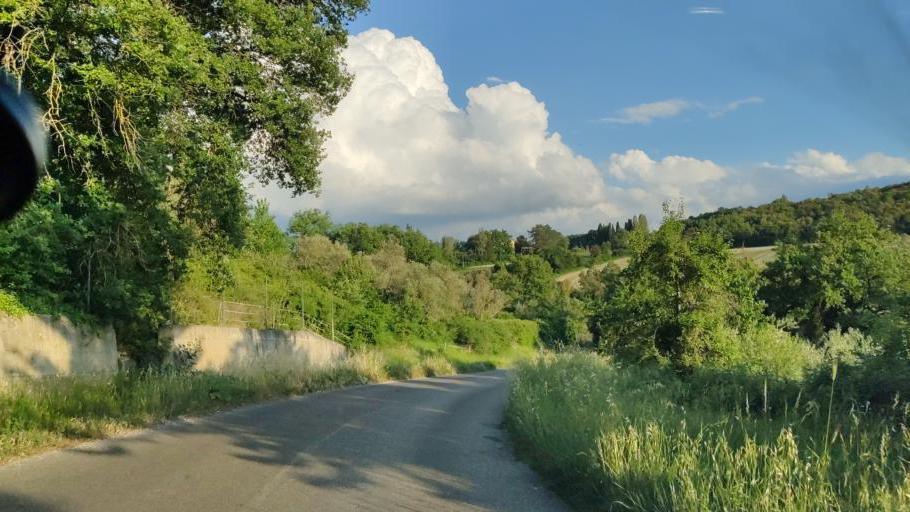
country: IT
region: Umbria
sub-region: Provincia di Terni
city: Amelia
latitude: 42.5734
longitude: 12.3996
